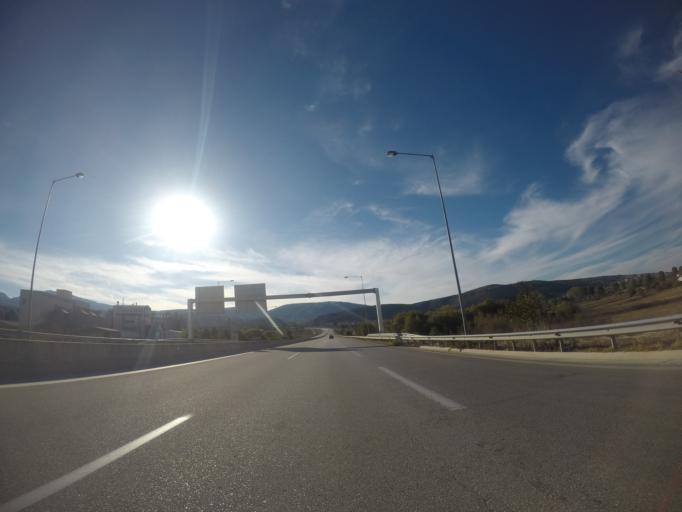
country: GR
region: Epirus
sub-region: Nomos Ioanninon
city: Pedini
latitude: 39.5949
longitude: 20.8576
